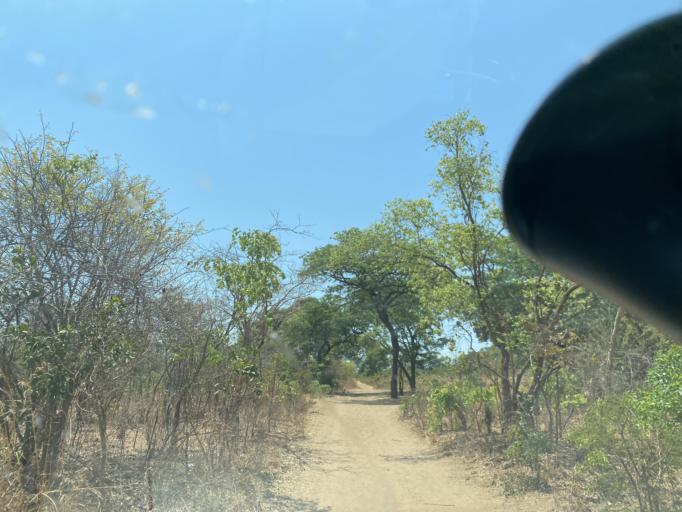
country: ZM
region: Lusaka
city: Chongwe
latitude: -15.4209
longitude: 29.1746
